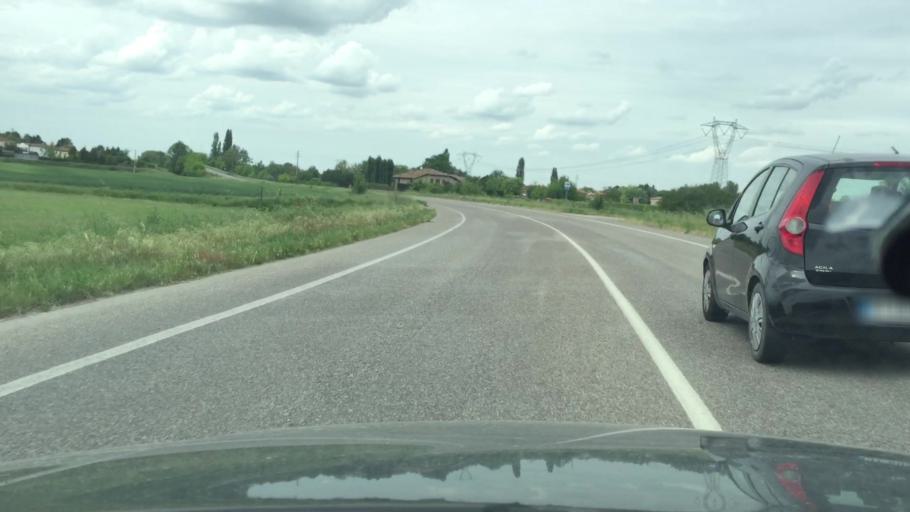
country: IT
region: Emilia-Romagna
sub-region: Provincia di Ferrara
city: Cona
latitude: 44.8088
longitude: 11.7182
